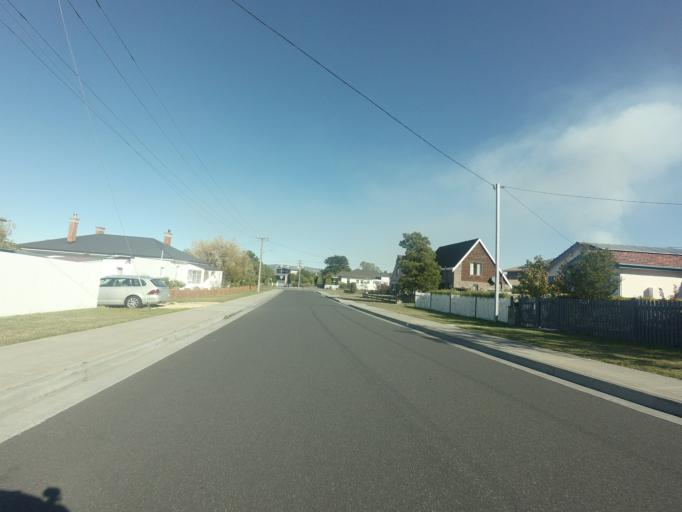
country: AU
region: Tasmania
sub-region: Clarence
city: Lindisfarne
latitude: -42.8487
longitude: 147.3466
